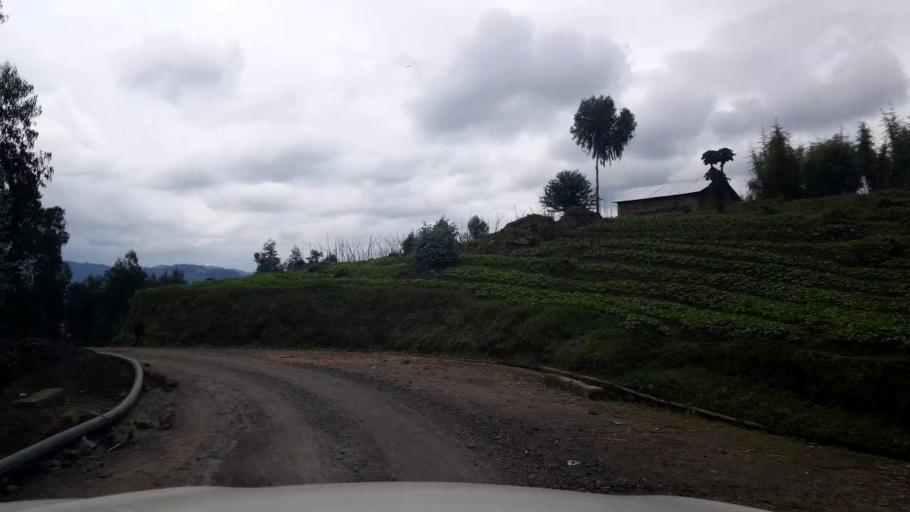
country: RW
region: Northern Province
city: Musanze
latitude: -1.5358
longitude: 29.5331
